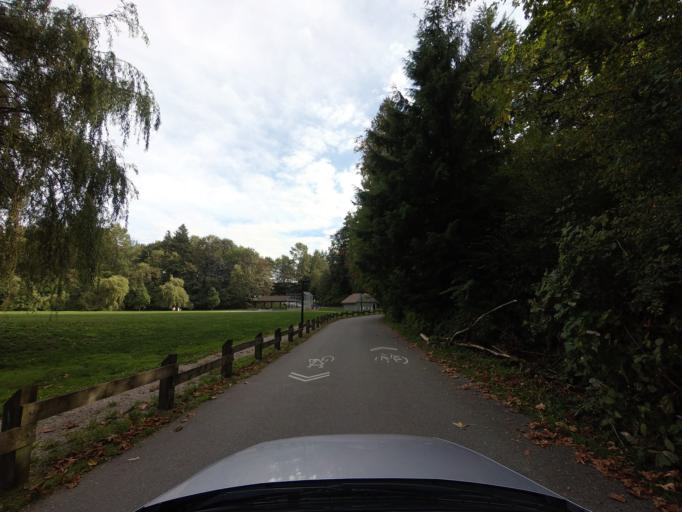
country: CA
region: British Columbia
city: New Westminster
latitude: 49.2363
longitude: -122.8920
